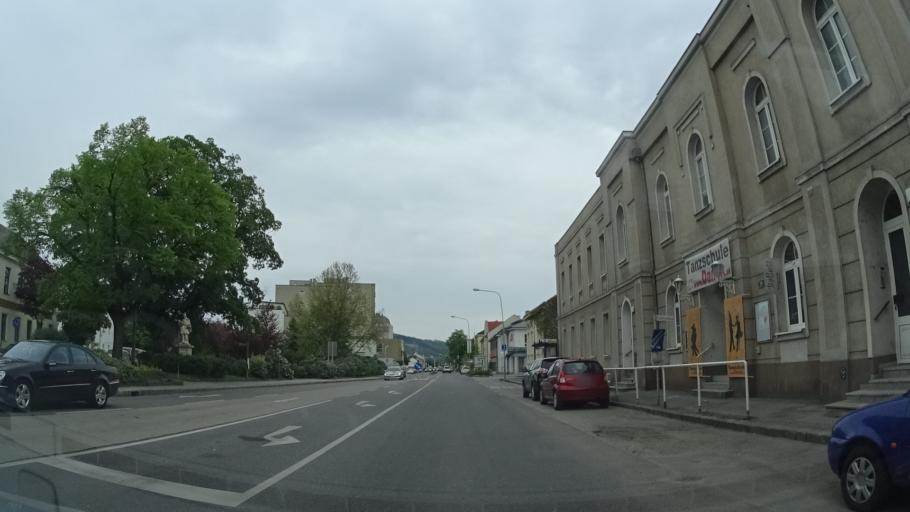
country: AT
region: Lower Austria
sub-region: Politischer Bezirk Korneuburg
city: Korneuburg
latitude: 48.3420
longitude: 16.3351
